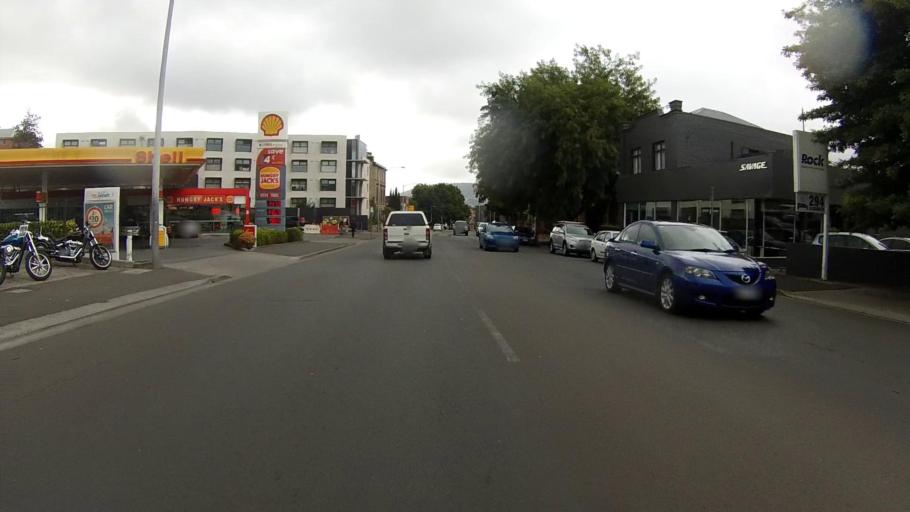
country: AU
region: Tasmania
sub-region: Hobart
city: Hobart
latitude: -42.8763
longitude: 147.3184
